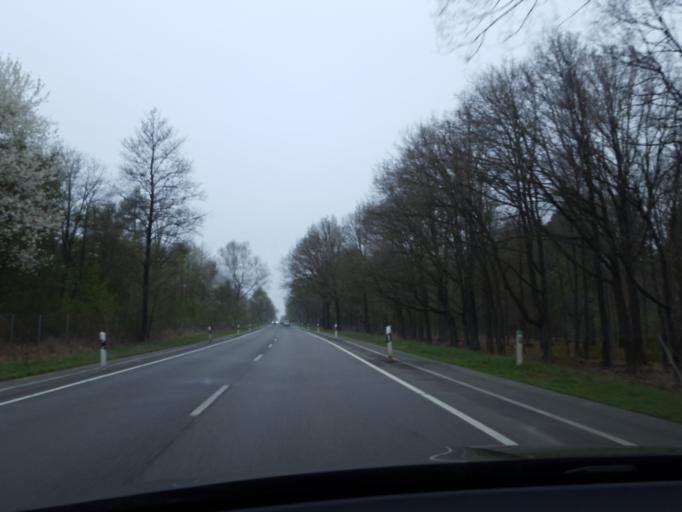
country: DE
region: North Rhine-Westphalia
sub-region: Regierungsbezirk Dusseldorf
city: Schermbeck
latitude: 51.7230
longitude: 6.9176
